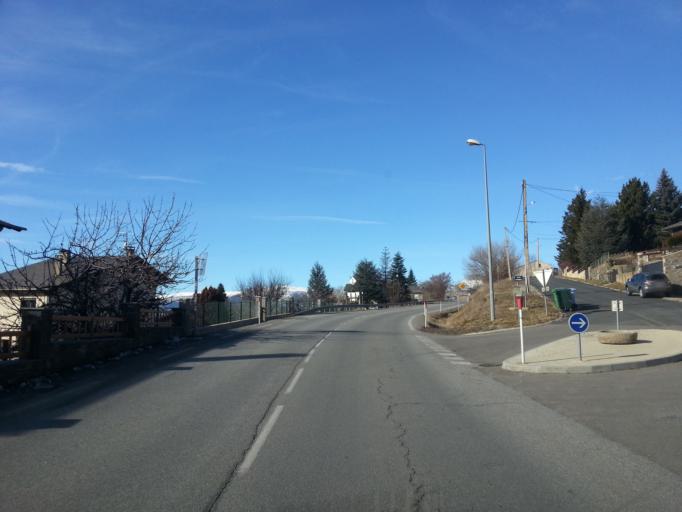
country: ES
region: Catalonia
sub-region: Provincia de Girona
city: Llivia
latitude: 42.4622
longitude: 2.0383
